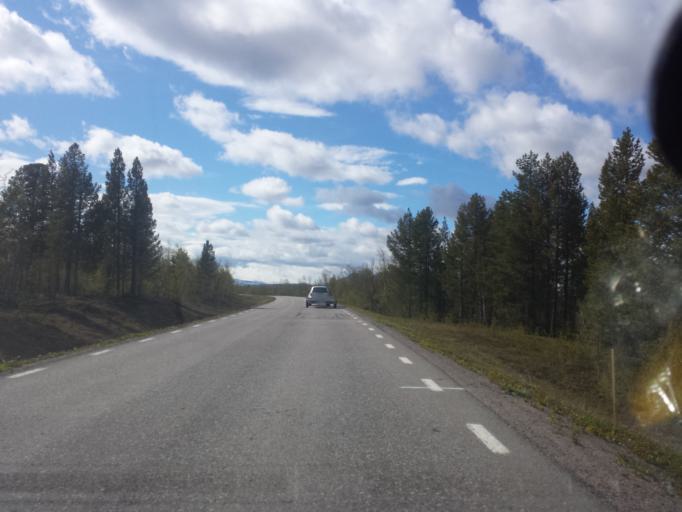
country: SE
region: Norrbotten
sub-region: Kiruna Kommun
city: Kiruna
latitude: 67.9942
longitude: 19.9054
